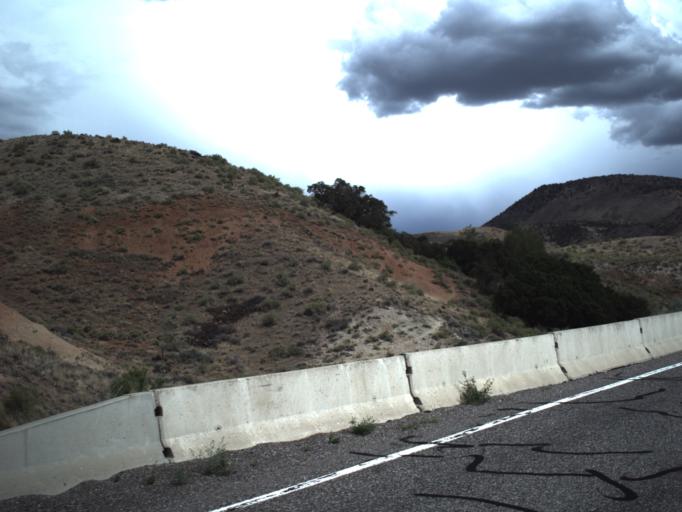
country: US
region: Utah
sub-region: Sevier County
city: Richfield
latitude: 38.7697
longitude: -111.9811
